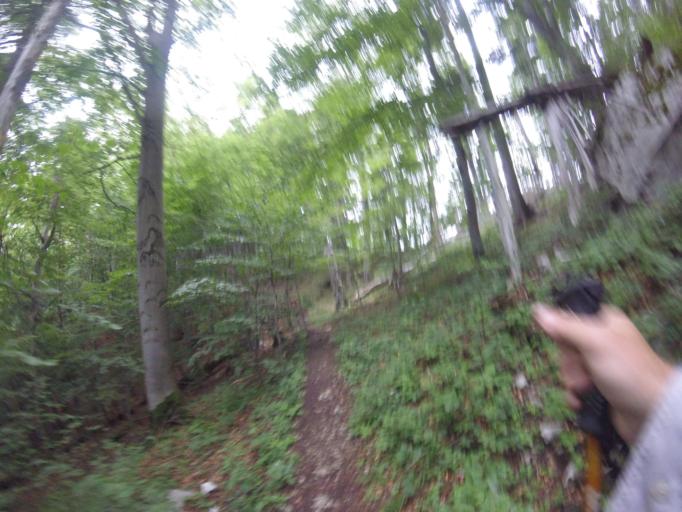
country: SK
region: Zilinsky
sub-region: Okres Zilina
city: Terchova
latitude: 49.2379
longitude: 19.0259
